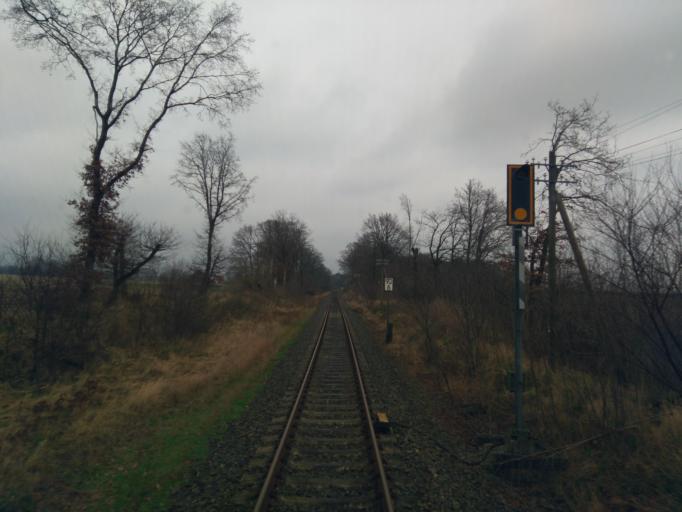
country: DE
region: Lower Saxony
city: Verden
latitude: 52.9585
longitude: 9.2543
